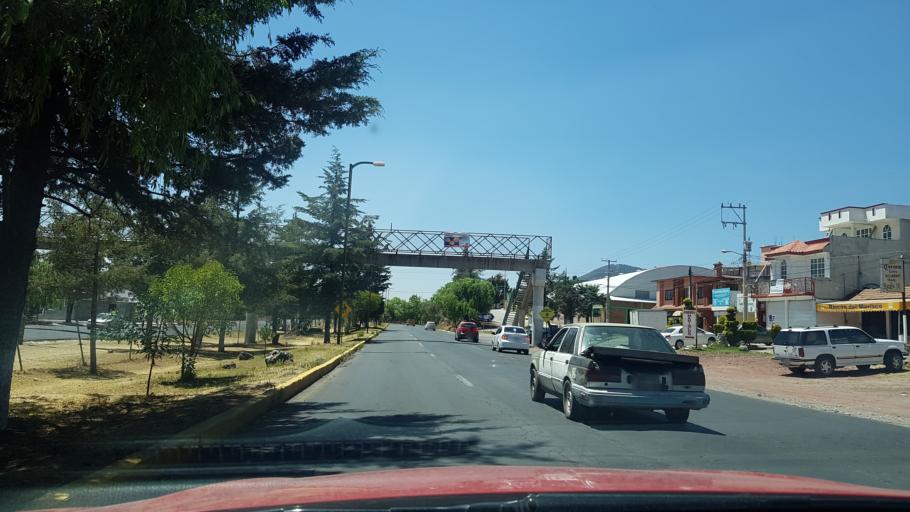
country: MX
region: Mexico
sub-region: Atlacomulco
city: Santa Cruz Bombatevi
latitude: 19.8016
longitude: -99.8859
